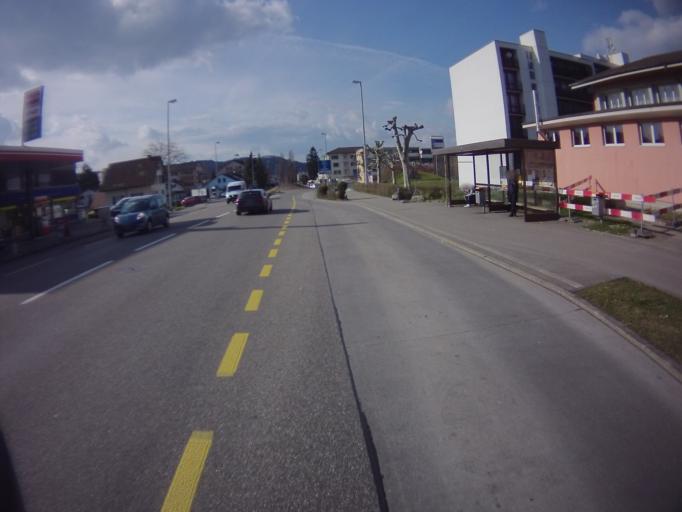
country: CH
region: Aargau
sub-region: Bezirk Baden
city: Neuenhof
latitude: 47.4515
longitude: 8.3249
